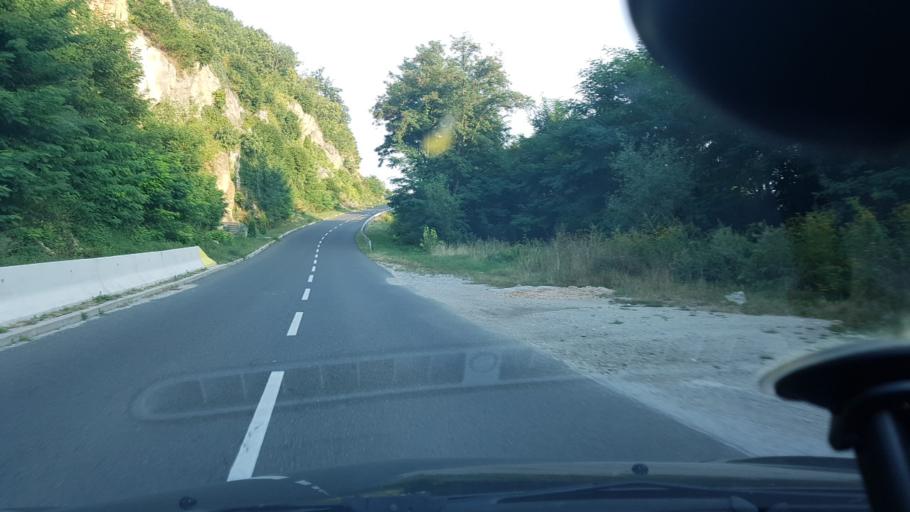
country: HR
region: Krapinsko-Zagorska
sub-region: Grad Krapina
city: Krapina
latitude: 46.1666
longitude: 15.8515
